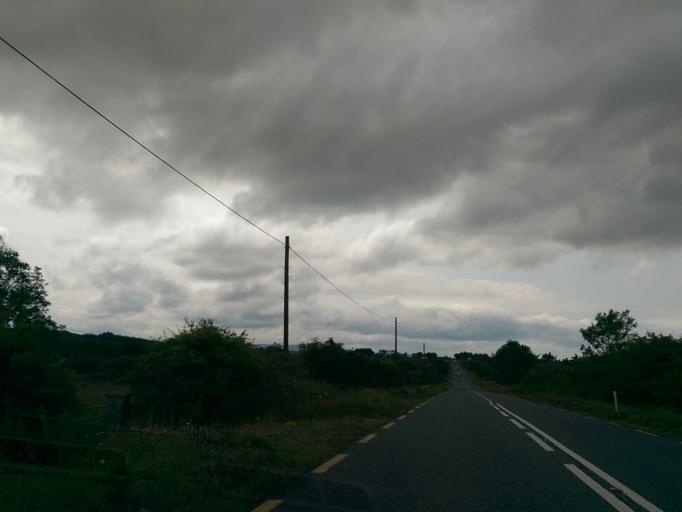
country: IE
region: Munster
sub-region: An Clar
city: Kilrush
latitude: 52.6687
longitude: -9.4008
